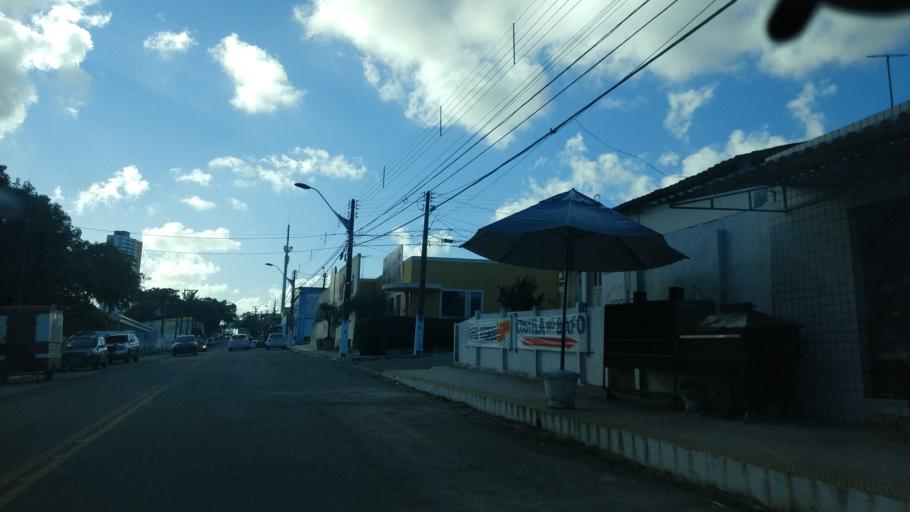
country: BR
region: Rio Grande do Norte
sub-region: Natal
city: Natal
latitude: -5.8444
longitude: -35.2083
